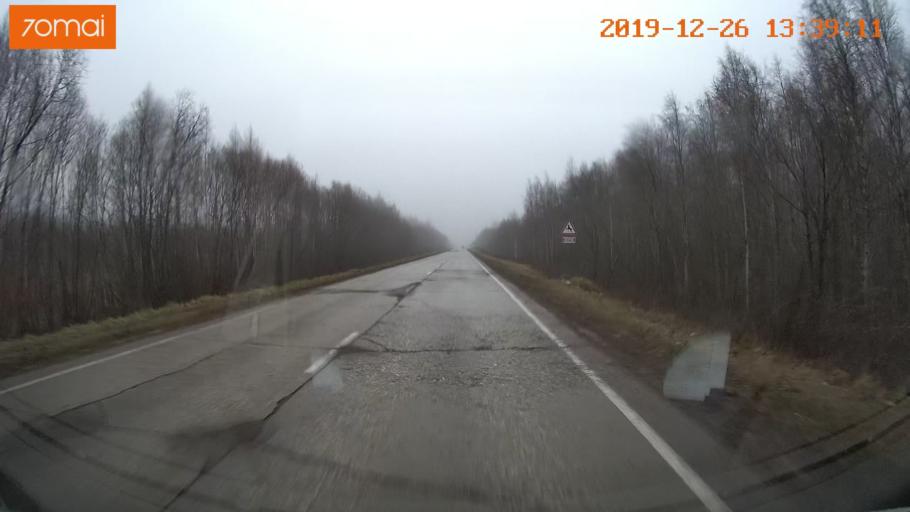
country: RU
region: Vologda
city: Sheksna
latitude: 58.7545
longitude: 38.4064
